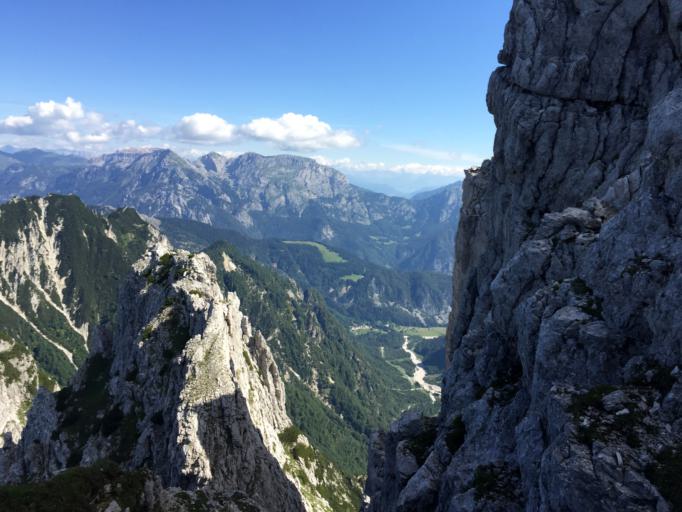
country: IT
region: Friuli Venezia Giulia
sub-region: Provincia di Udine
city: Pontebba
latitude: 46.4702
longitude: 13.2460
